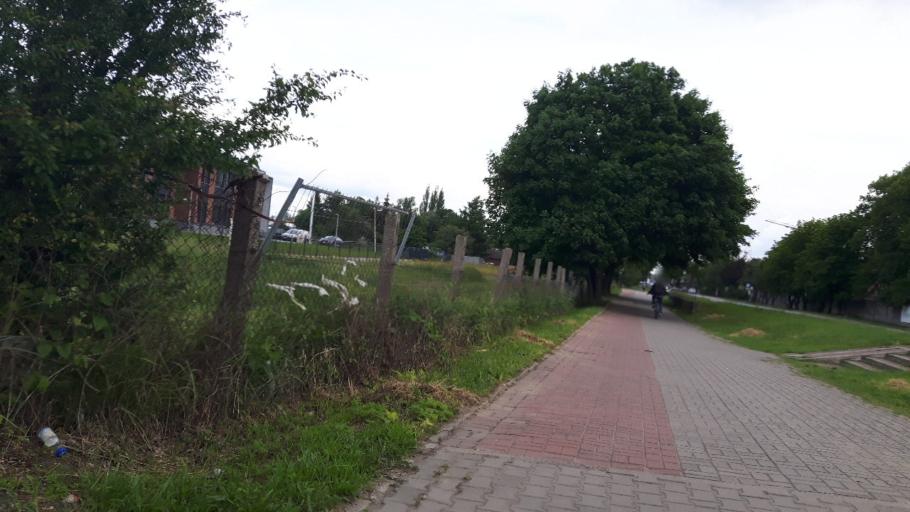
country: PL
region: West Pomeranian Voivodeship
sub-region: Powiat policki
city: Przeclaw
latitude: 53.3946
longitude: 14.4901
